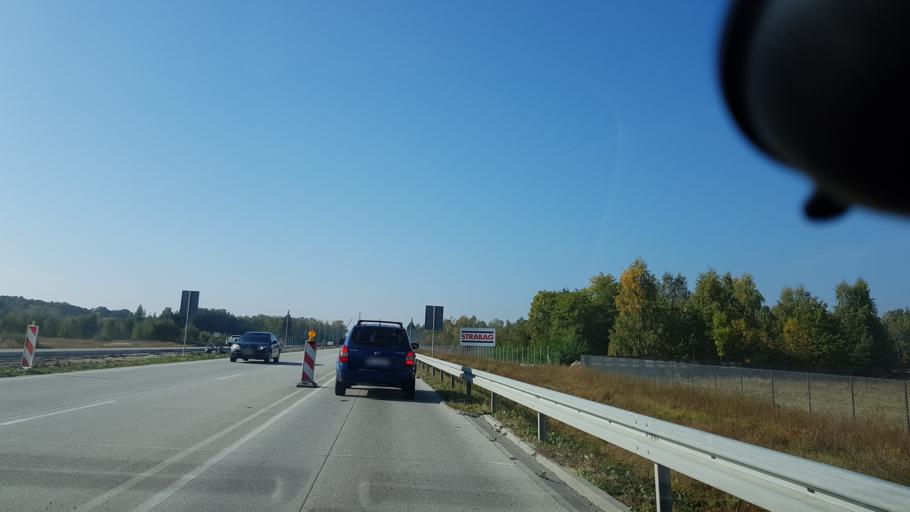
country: PL
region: Lodz Voivodeship
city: Zabia Wola
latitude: 52.0344
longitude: 20.6881
